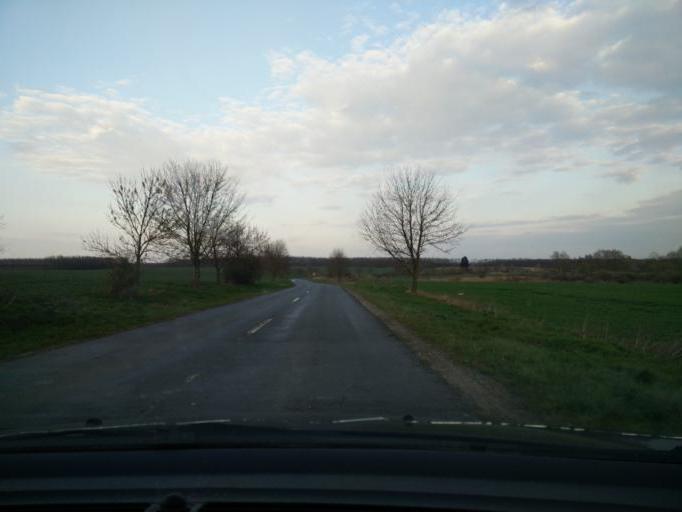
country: HU
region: Zala
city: Turje
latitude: 46.9945
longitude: 17.0516
